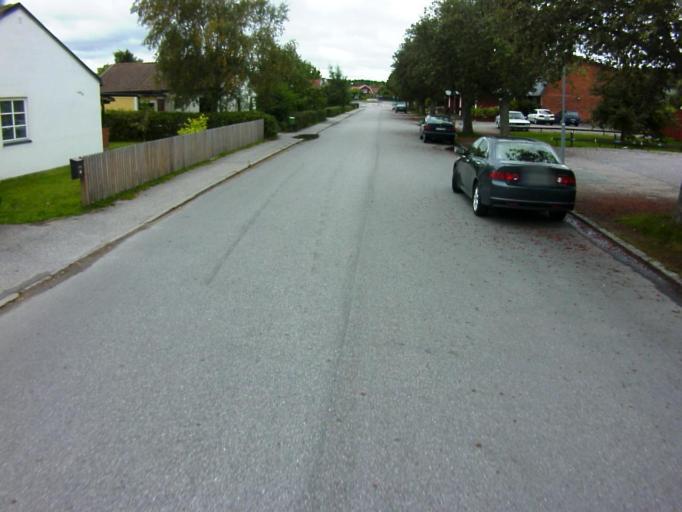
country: SE
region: Soedermanland
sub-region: Eskilstuna Kommun
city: Eskilstuna
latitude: 59.3774
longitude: 16.4784
